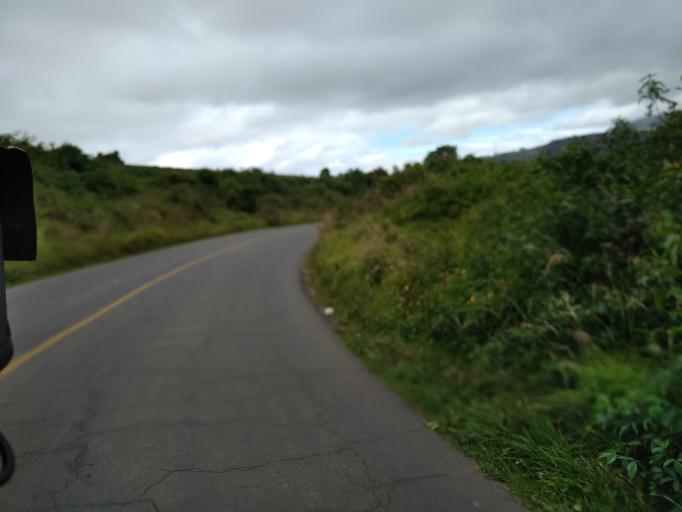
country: EC
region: Carchi
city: El Angel
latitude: 0.6281
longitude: -77.9317
